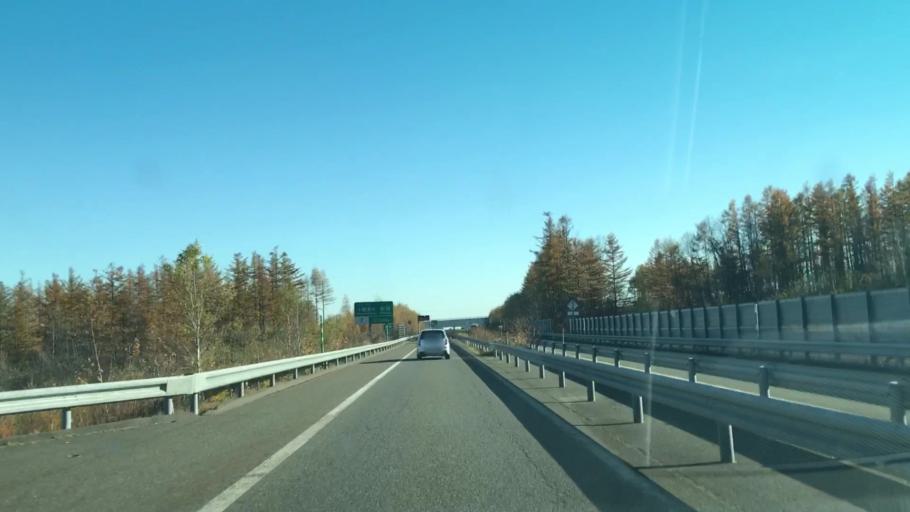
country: JP
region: Hokkaido
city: Otofuke
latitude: 43.0007
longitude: 142.8495
